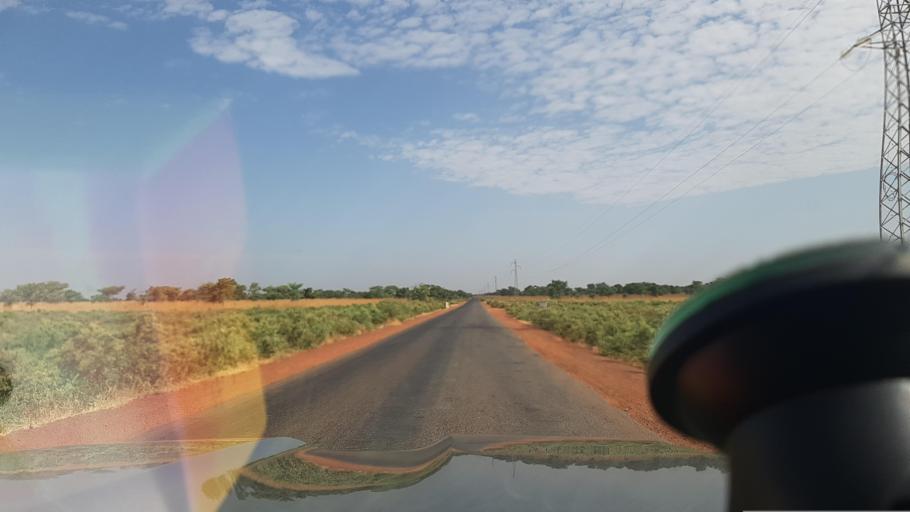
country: ML
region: Segou
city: Segou
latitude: 13.5519
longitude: -6.1162
